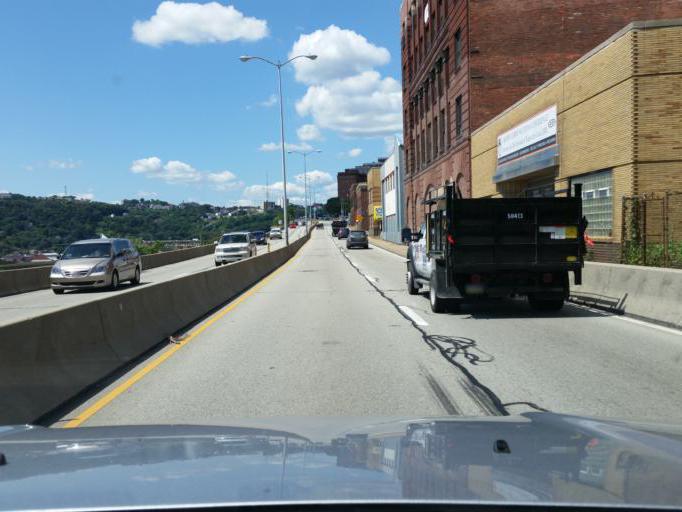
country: US
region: Pennsylvania
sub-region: Allegheny County
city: Pittsburgh
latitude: 40.4360
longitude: -79.9800
